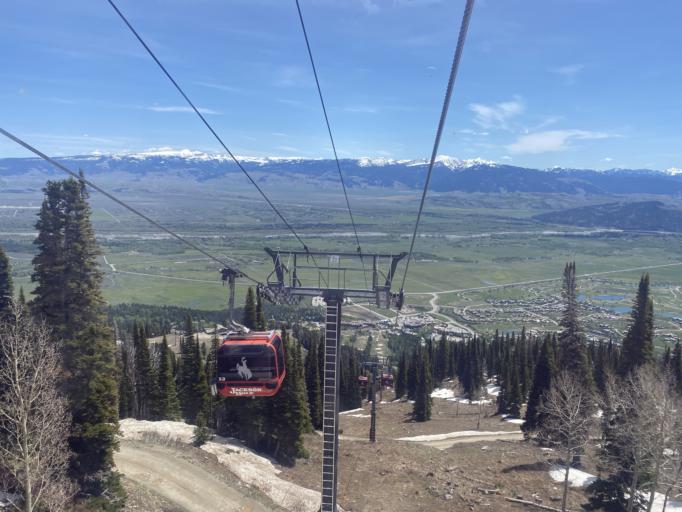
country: US
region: Wyoming
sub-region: Teton County
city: Moose Wilson Road
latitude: 43.5994
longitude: -110.8494
